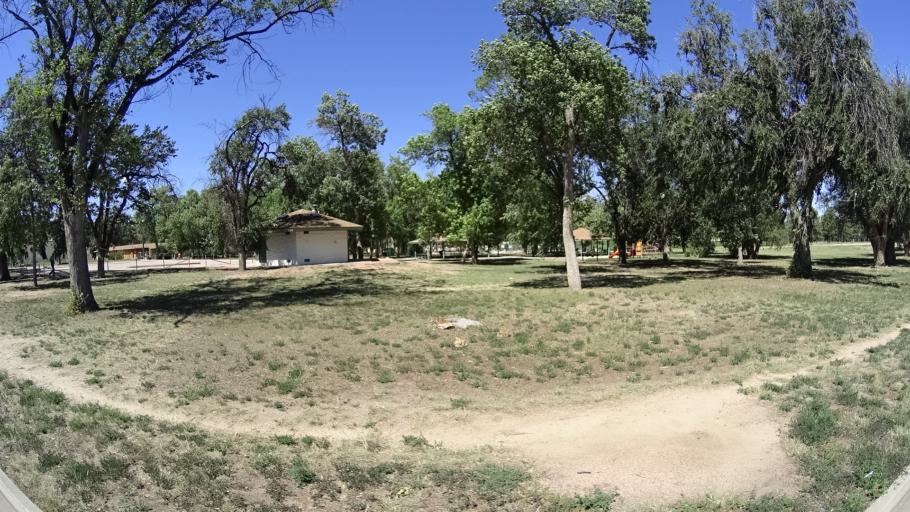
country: US
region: Colorado
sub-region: El Paso County
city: Colorado Springs
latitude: 38.8277
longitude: -104.8024
